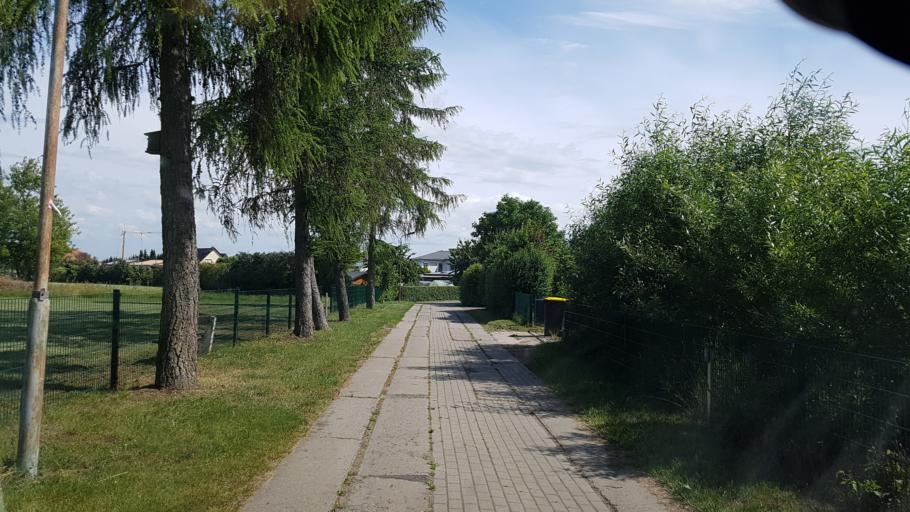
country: DE
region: Brandenburg
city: Gramzow
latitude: 53.2368
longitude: 13.9859
